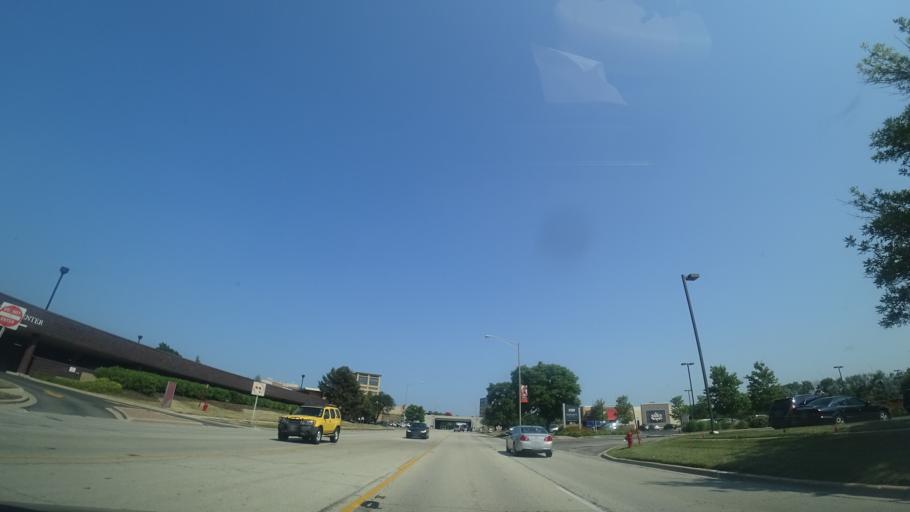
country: US
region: Illinois
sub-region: Cook County
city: Rosemont
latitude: 41.9942
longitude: -87.8695
